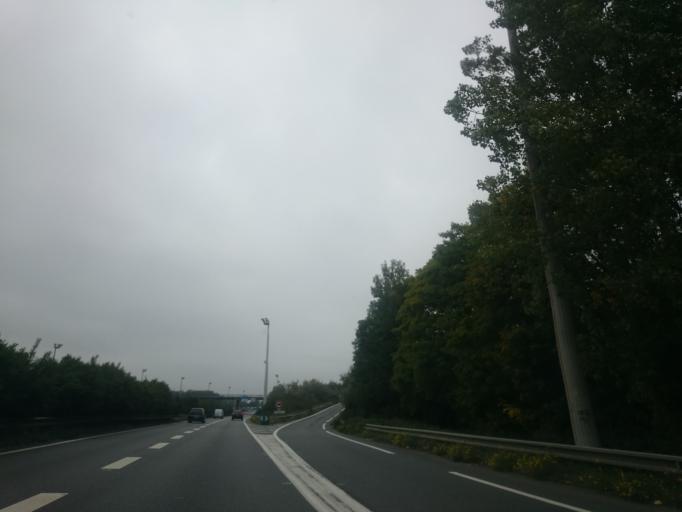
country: FR
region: Ile-de-France
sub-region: Departement de l'Essonne
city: Grigny
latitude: 48.6375
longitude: 2.3984
